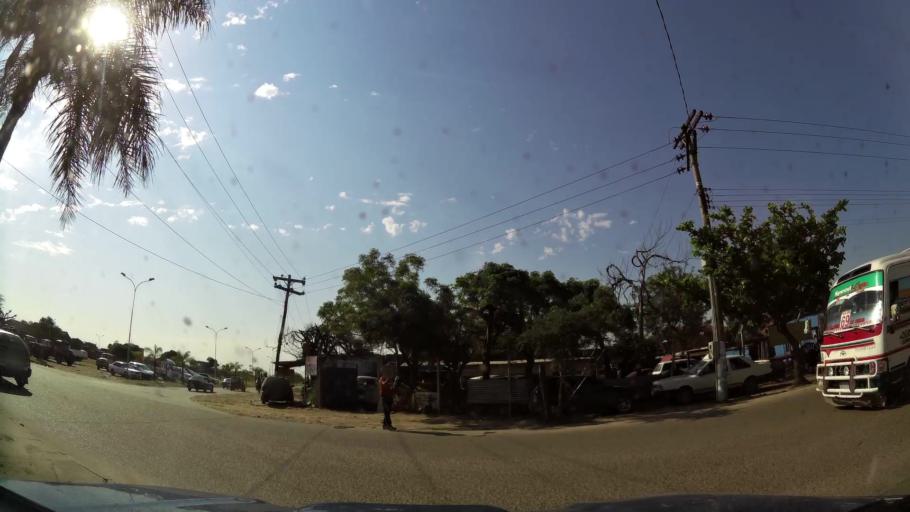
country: BO
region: Santa Cruz
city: Santa Cruz de la Sierra
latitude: -17.8005
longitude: -63.1418
